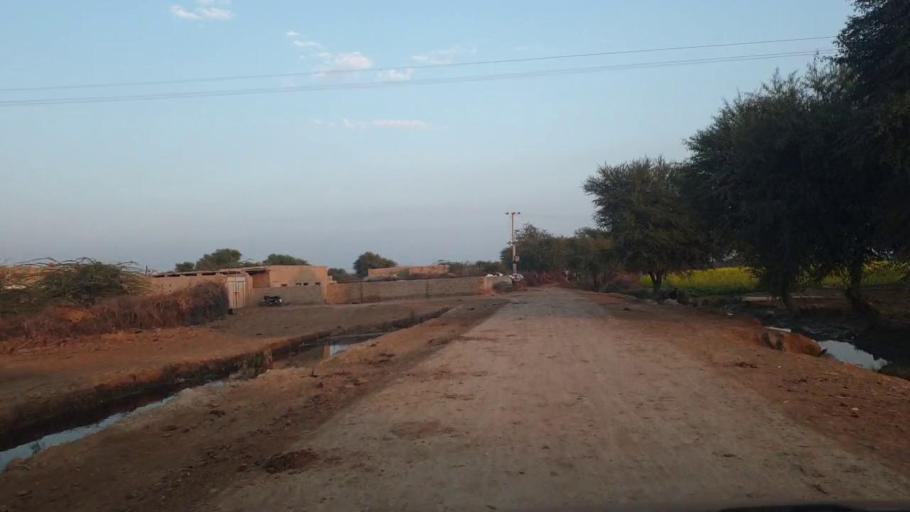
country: PK
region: Sindh
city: Berani
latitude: 25.8296
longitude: 68.7476
